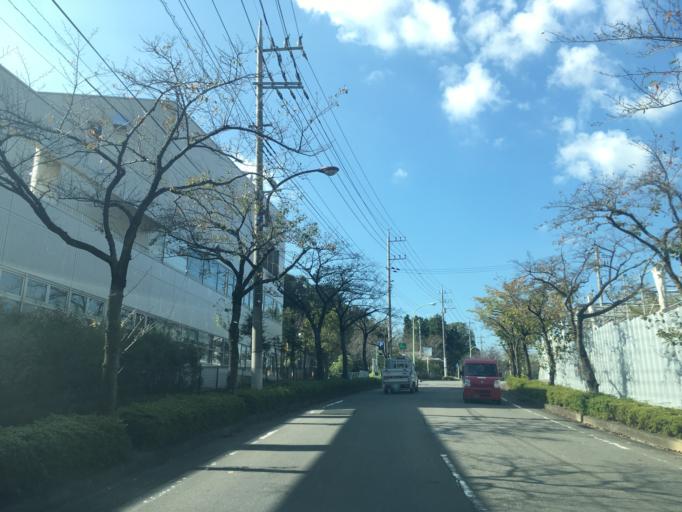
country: JP
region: Tokyo
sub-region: Machida-shi
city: Machida
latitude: 35.5866
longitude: 139.4138
